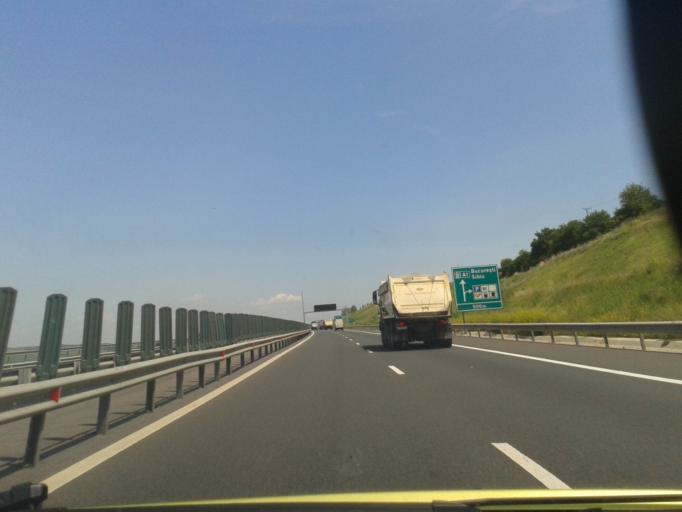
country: RO
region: Alba
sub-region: Comuna Cut
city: Cut
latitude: 45.9207
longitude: 23.6442
